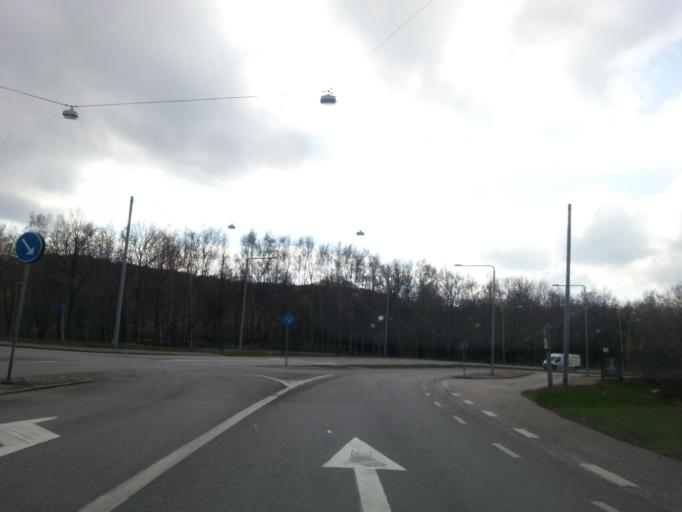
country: SE
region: Vaestra Goetaland
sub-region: Goteborg
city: Gardsten
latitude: 57.7875
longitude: 12.0019
